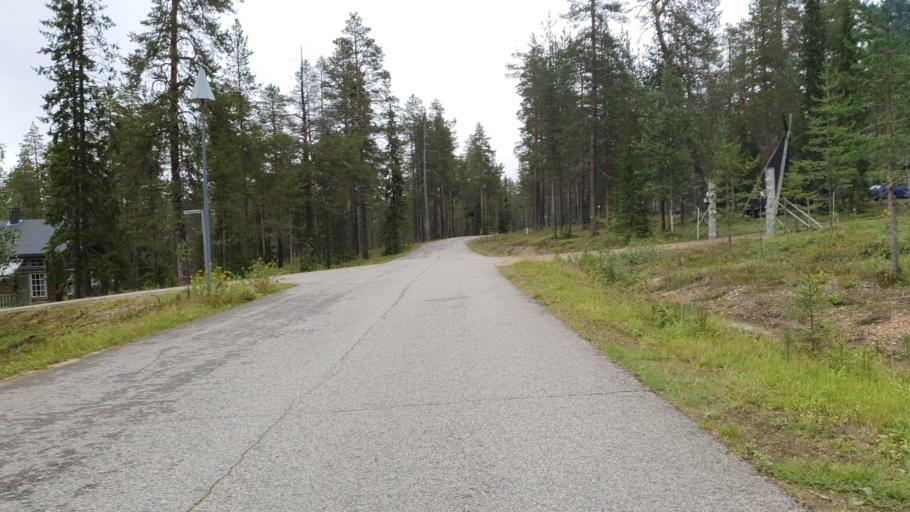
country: FI
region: Lapland
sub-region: Tunturi-Lappi
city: Kolari
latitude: 67.5990
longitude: 24.1846
